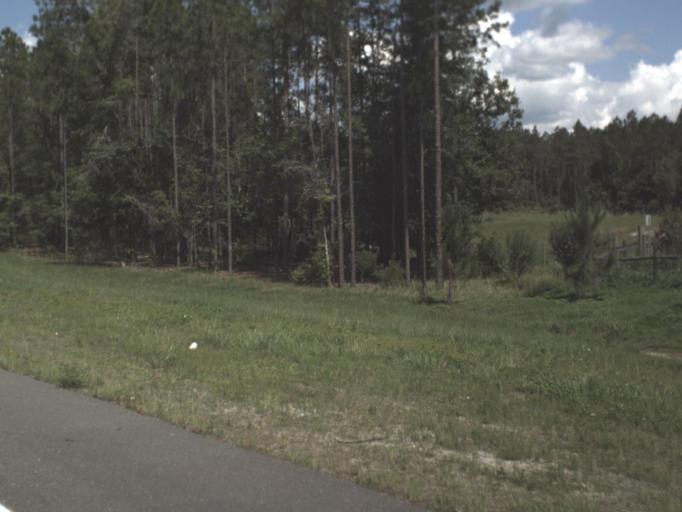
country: US
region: Florida
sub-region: Alachua County
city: Waldo
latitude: 29.7158
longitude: -82.1354
